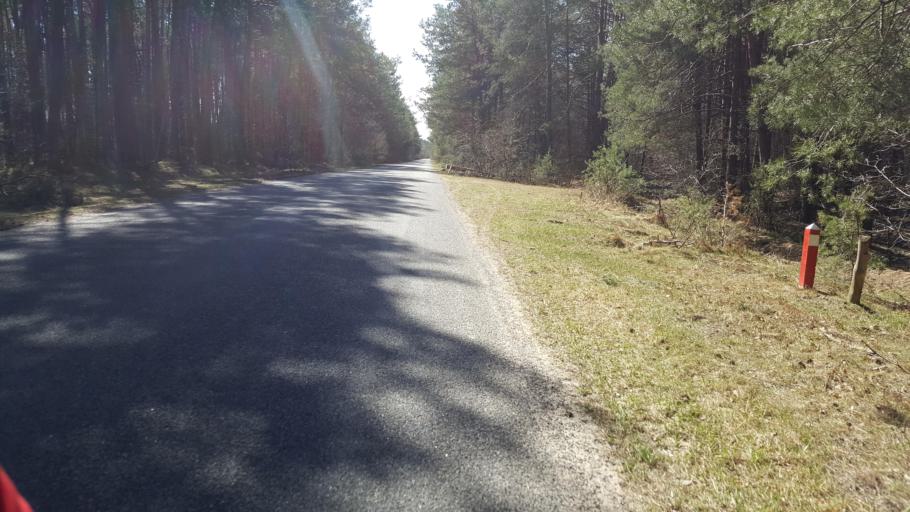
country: BY
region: Brest
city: Kamyanyets
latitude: 52.2958
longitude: 23.8224
